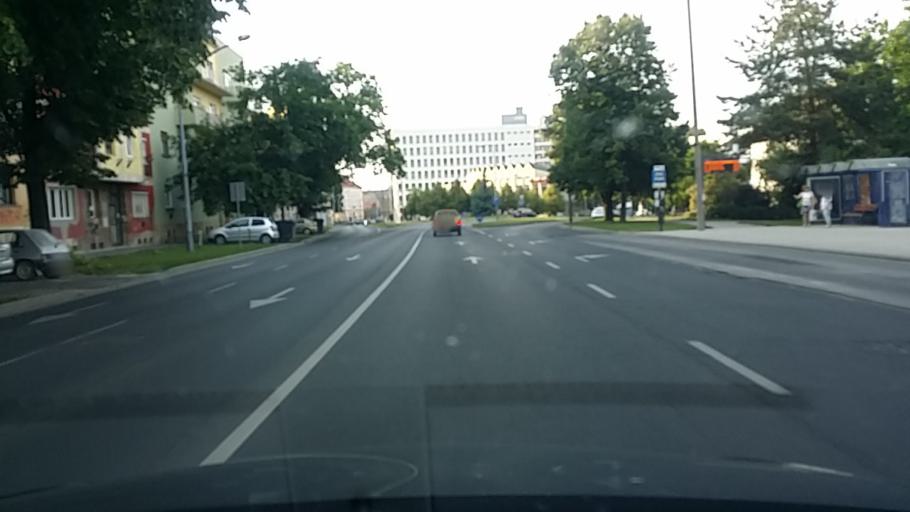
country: HU
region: Borsod-Abauj-Zemplen
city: Miskolc
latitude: 48.0966
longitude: 20.7857
